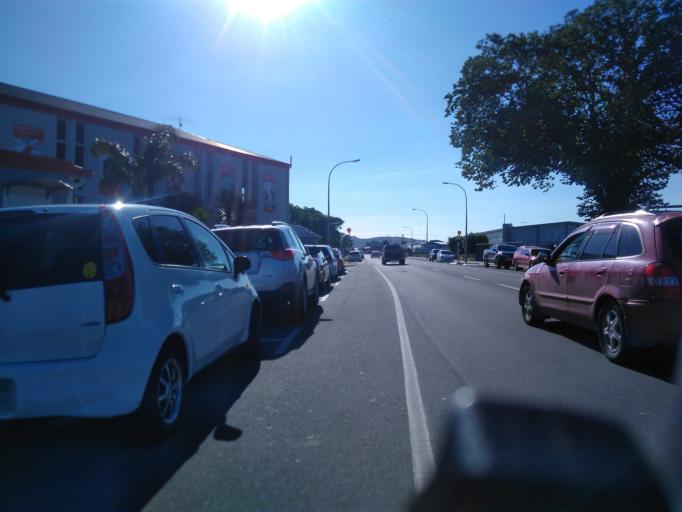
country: NZ
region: Gisborne
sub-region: Gisborne District
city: Gisborne
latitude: -38.6611
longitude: 178.0126
